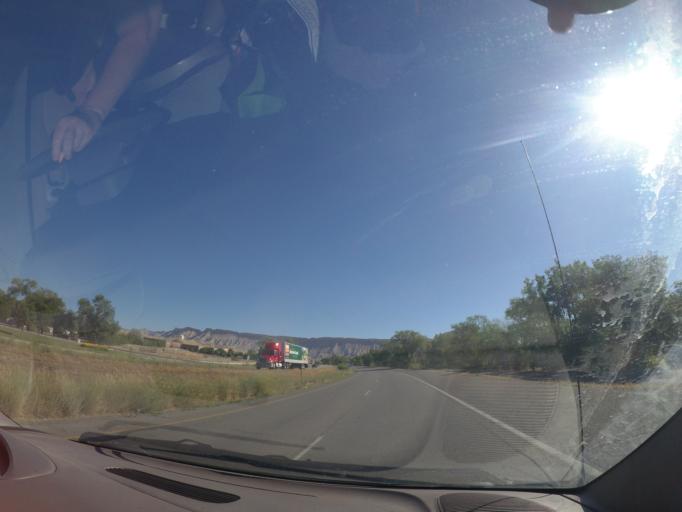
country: US
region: Colorado
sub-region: Mesa County
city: Clifton
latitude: 39.0941
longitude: -108.4507
